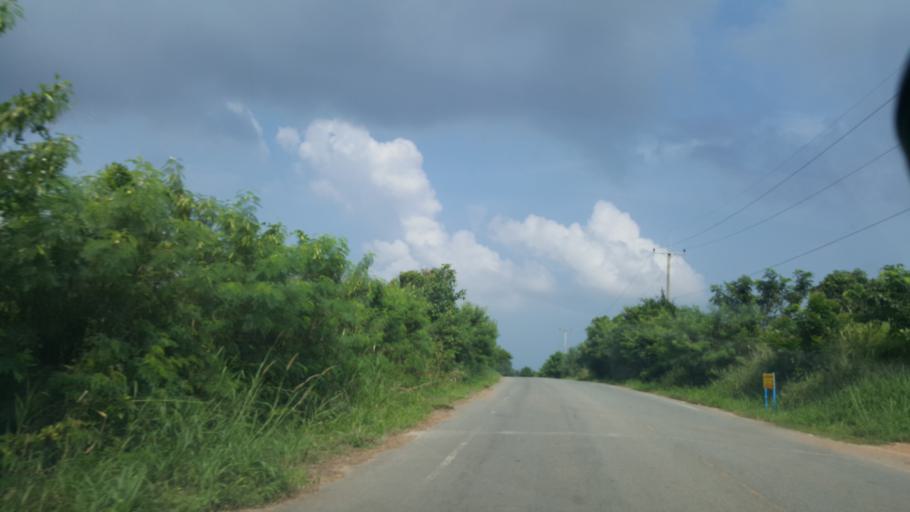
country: TH
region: Chon Buri
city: Sattahip
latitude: 12.7208
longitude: 100.9173
